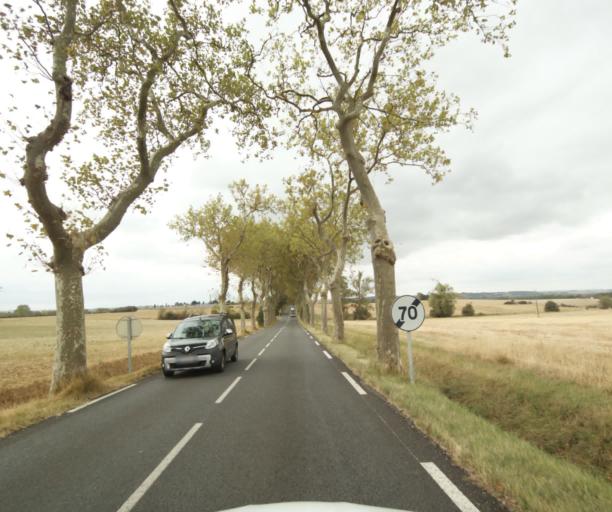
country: FR
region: Midi-Pyrenees
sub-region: Departement de la Haute-Garonne
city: Villefranche-de-Lauragais
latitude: 43.4084
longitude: 1.7319
